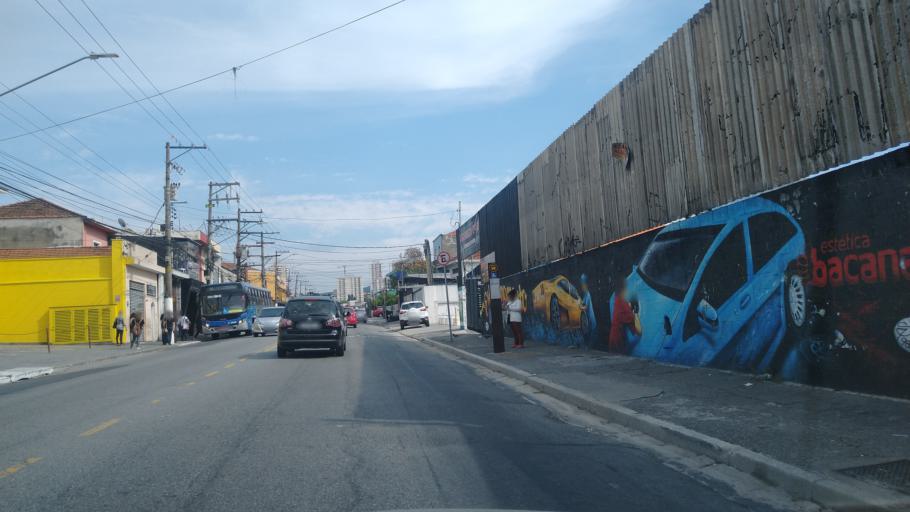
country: BR
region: Sao Paulo
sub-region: Sao Paulo
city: Sao Paulo
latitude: -23.4842
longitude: -46.6534
